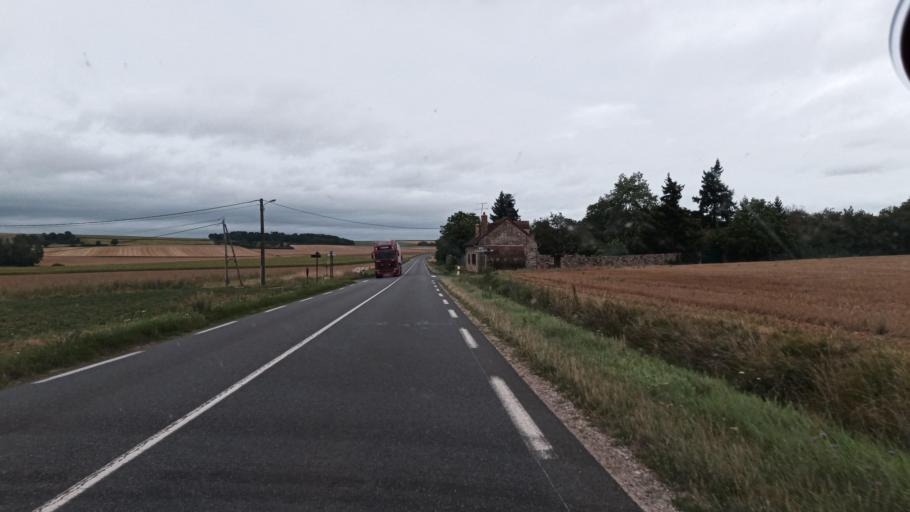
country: FR
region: Ile-de-France
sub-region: Departement de Seine-et-Marne
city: Voulx
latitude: 48.3075
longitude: 2.9476
